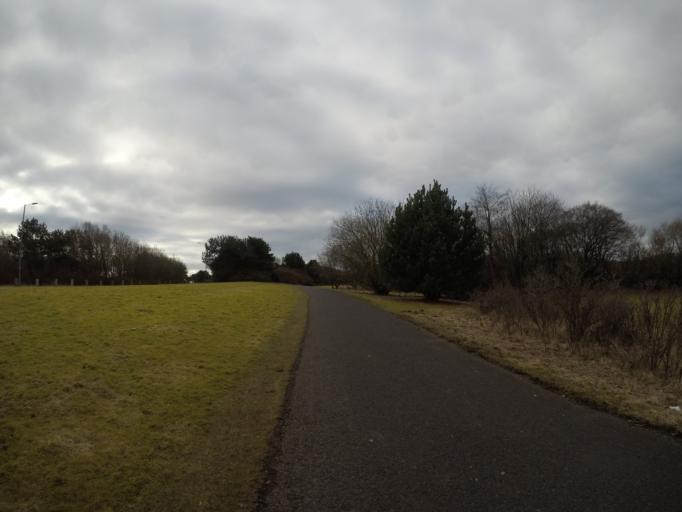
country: GB
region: Scotland
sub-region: North Ayrshire
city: Irvine
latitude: 55.6036
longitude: -4.6809
